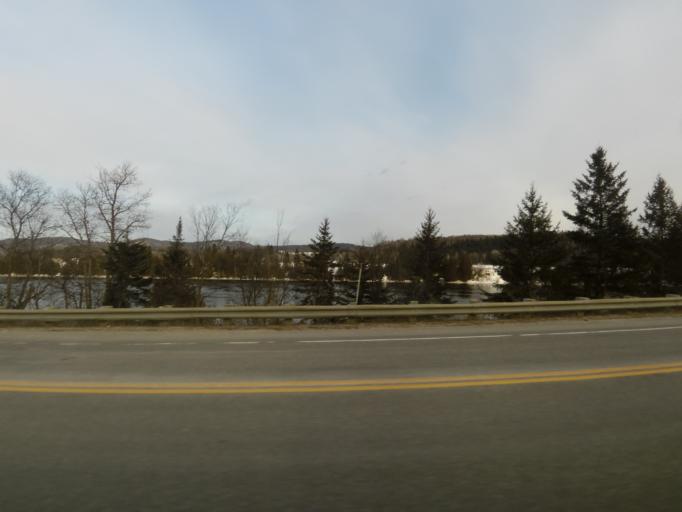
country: CA
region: Quebec
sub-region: Outaouais
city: Wakefield
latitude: 45.7152
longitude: -75.9168
